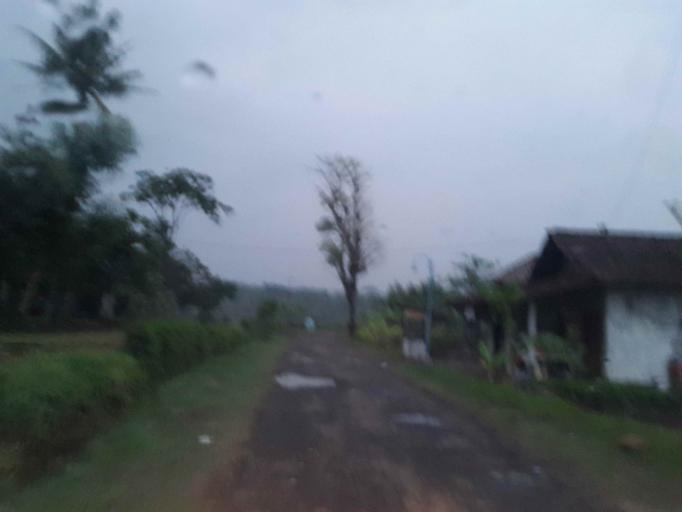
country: ID
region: Central Java
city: Jaten
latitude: -7.5555
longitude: 111.0166
